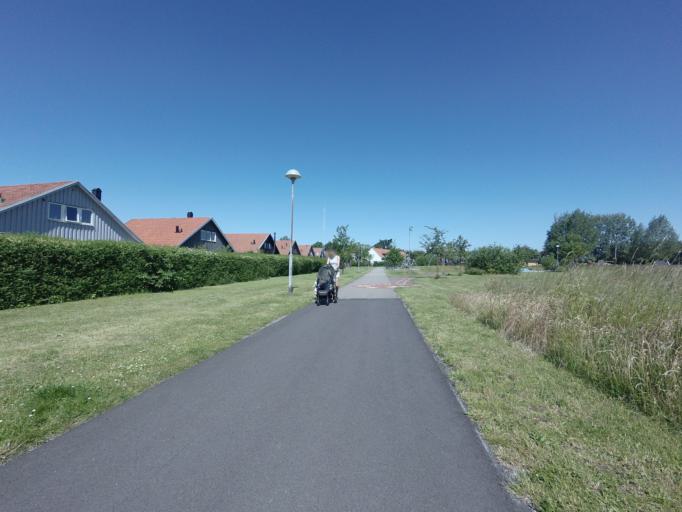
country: SE
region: Skane
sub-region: Vellinge Kommun
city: Hollviken
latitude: 55.4197
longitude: 12.9739
